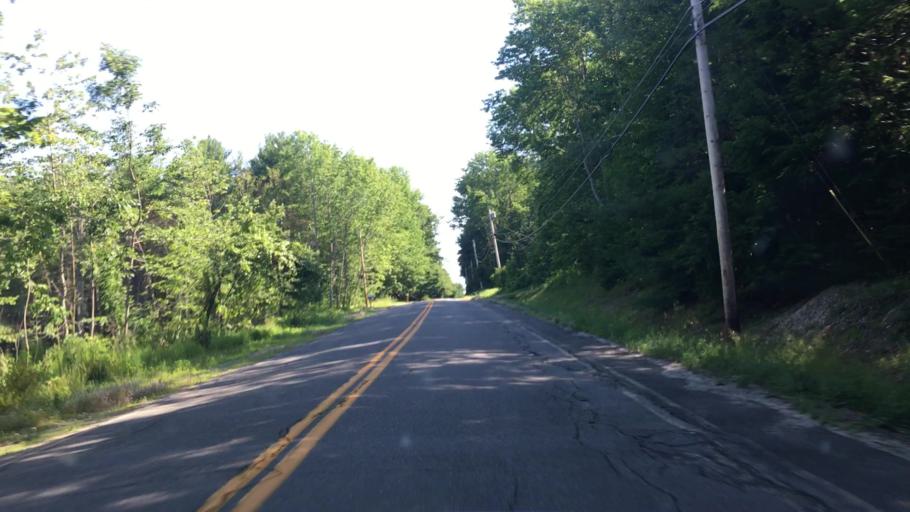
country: US
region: Maine
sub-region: Penobscot County
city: Enfield
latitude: 45.2684
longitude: -68.5618
